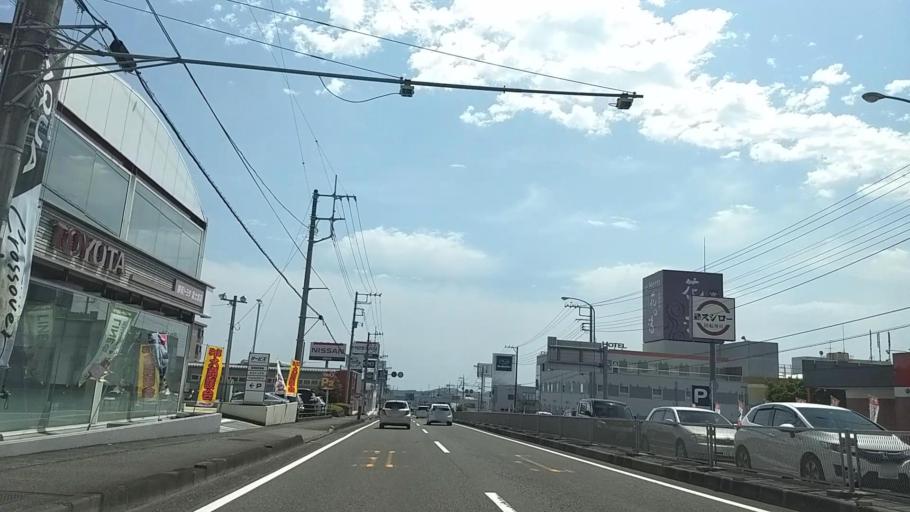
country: JP
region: Shizuoka
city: Fujinomiya
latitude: 35.2398
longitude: 138.6195
